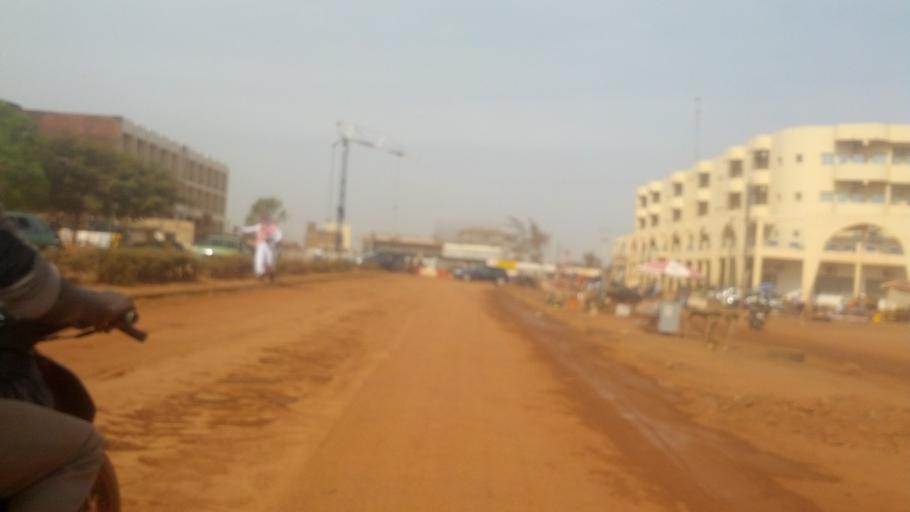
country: BF
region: Centre
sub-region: Kadiogo Province
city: Ouagadougou
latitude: 12.3869
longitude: -1.5618
